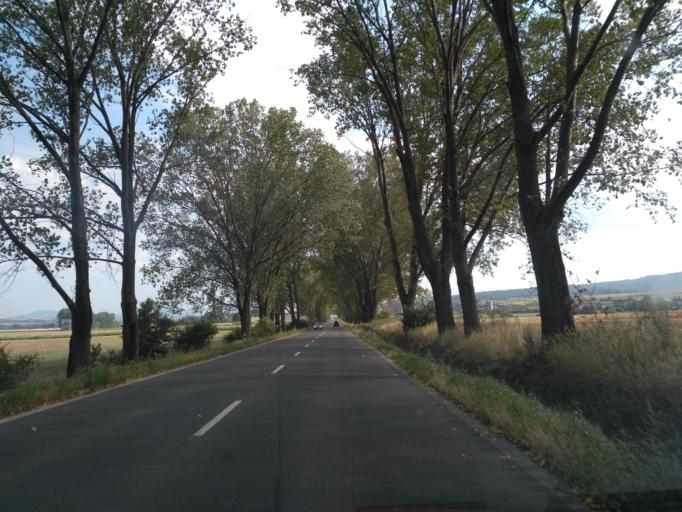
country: SK
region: Kosicky
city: Kosice
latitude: 48.8142
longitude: 21.3000
